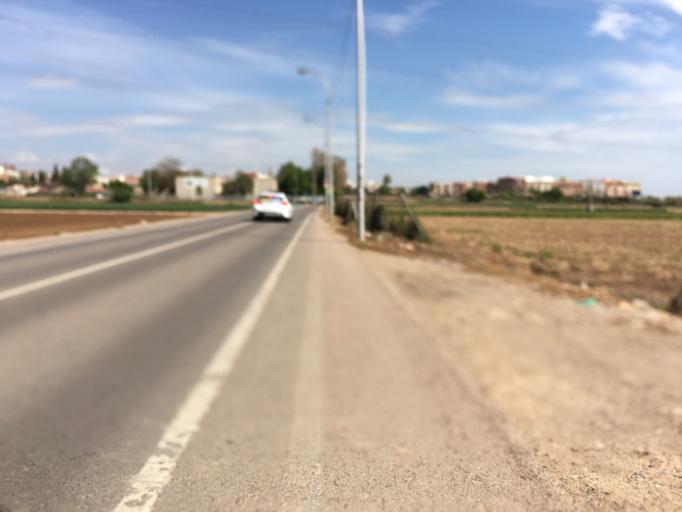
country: ES
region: Valencia
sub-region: Provincia de Valencia
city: Paterna
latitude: 39.4923
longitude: -0.4181
